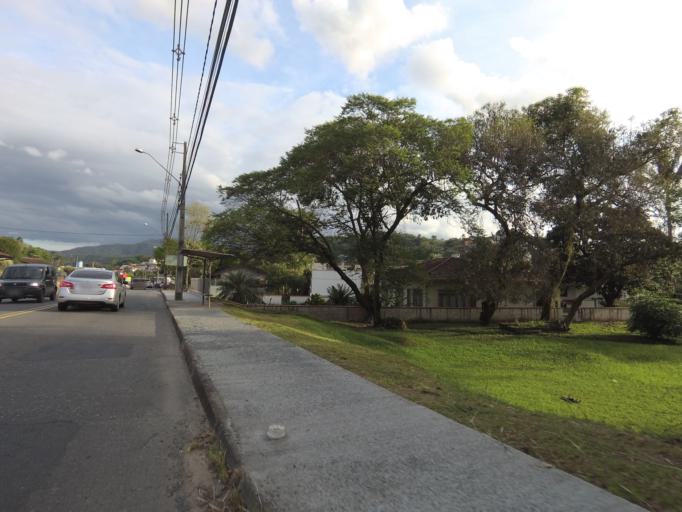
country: BR
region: Santa Catarina
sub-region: Blumenau
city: Blumenau
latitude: -26.9076
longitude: -49.1224
